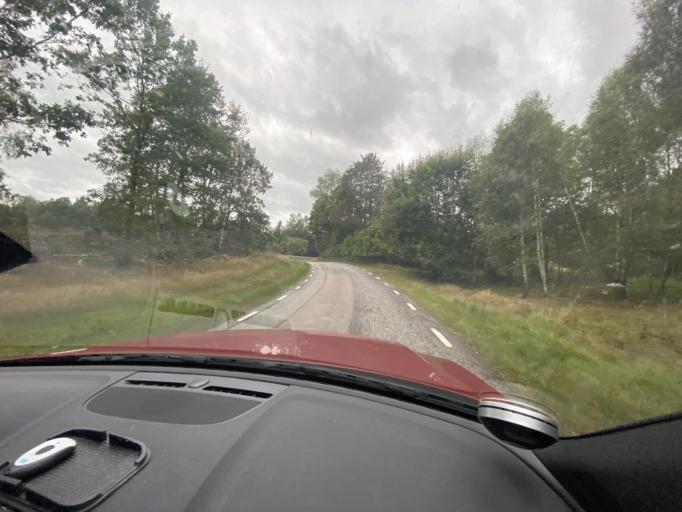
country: SE
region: Kronoberg
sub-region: Markaryds Kommun
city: Markaryd
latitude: 56.4978
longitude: 13.5319
